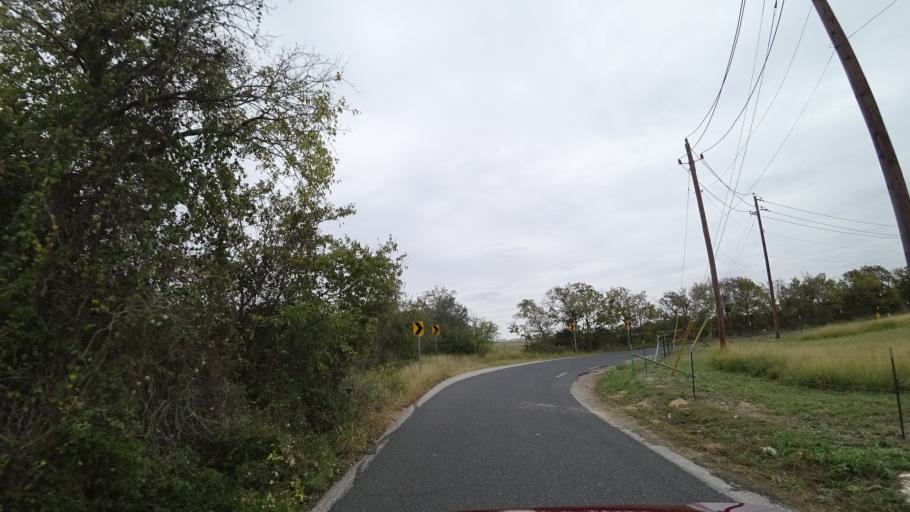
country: US
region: Texas
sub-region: Travis County
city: Wells Branch
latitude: 30.4493
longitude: -97.7042
